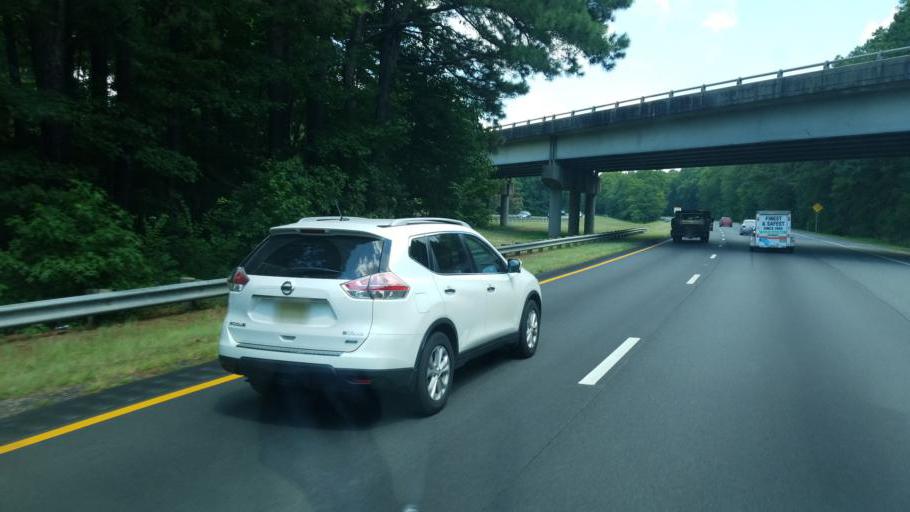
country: US
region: Virginia
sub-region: City of Suffolk
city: Suffolk
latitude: 36.7523
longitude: -76.5244
